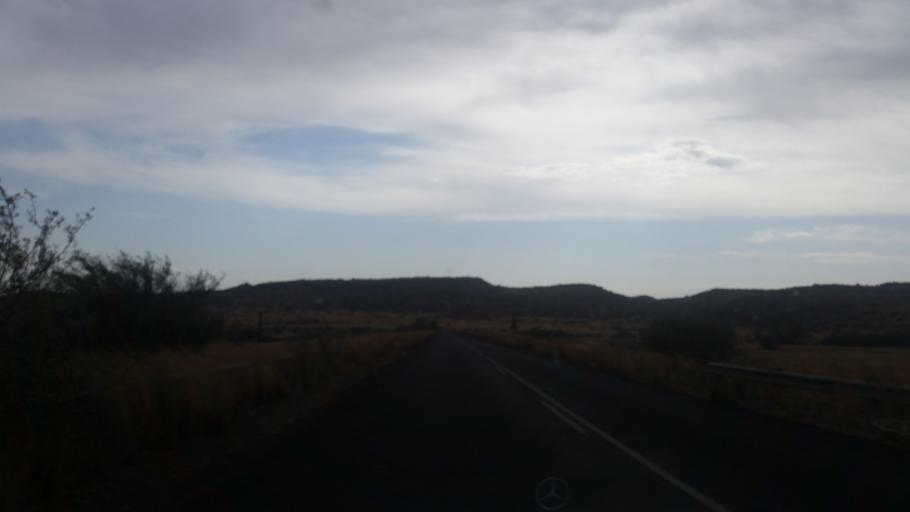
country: ZA
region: Orange Free State
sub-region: Xhariep District Municipality
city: Trompsburg
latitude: -30.4257
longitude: 26.1156
